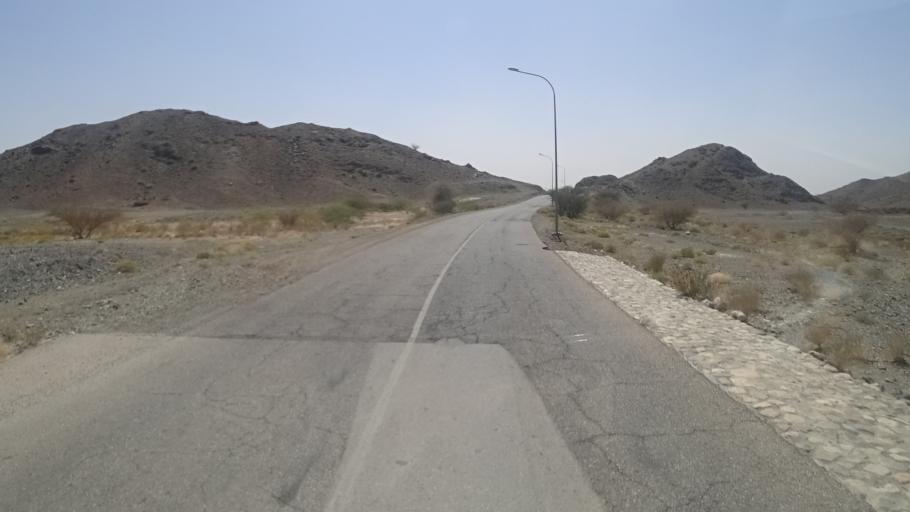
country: OM
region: Ash Sharqiyah
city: Ibra'
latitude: 22.6671
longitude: 58.5305
